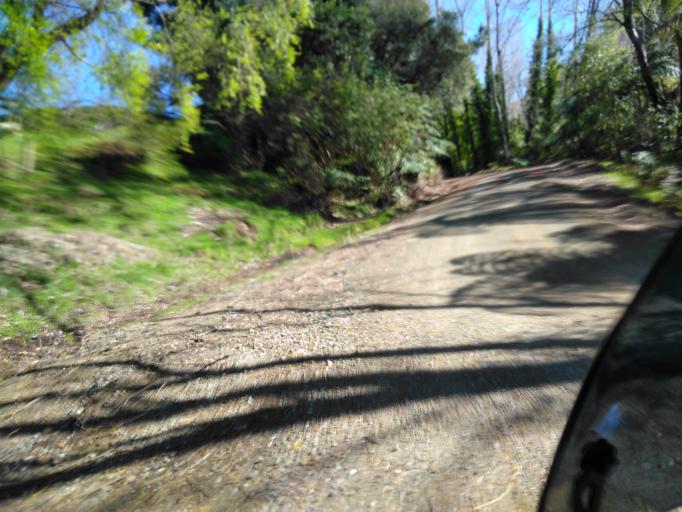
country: NZ
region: Bay of Plenty
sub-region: Opotiki District
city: Opotiki
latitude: -38.3700
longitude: 177.6007
